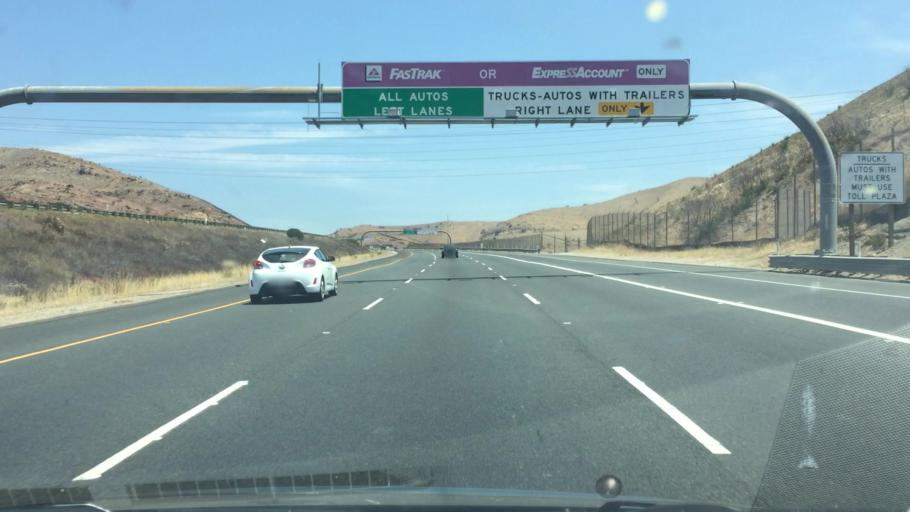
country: US
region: California
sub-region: Orange County
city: North Tustin
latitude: 33.8131
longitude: -117.7200
